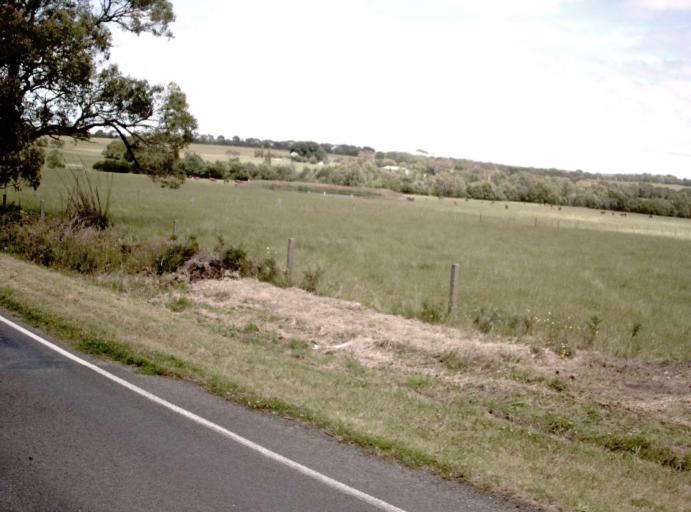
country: AU
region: Victoria
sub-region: Bass Coast
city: North Wonthaggi
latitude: -38.6253
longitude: 146.0141
